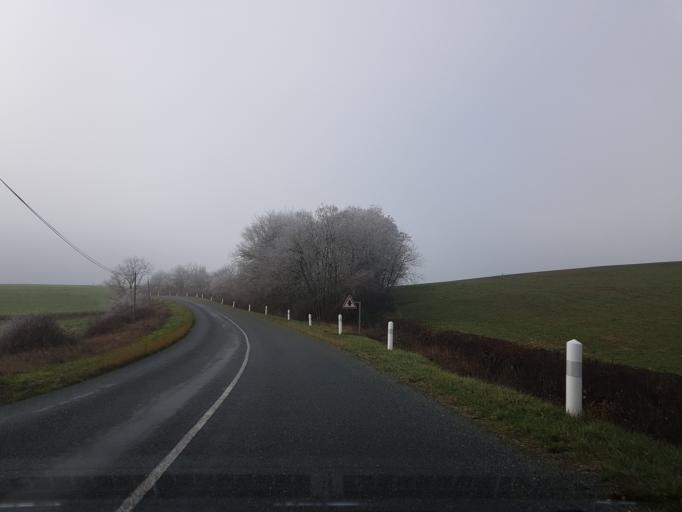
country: FR
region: Bourgogne
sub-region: Departement de Saone-et-Loire
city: Toulon-sur-Arroux
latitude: 46.7040
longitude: 4.2024
